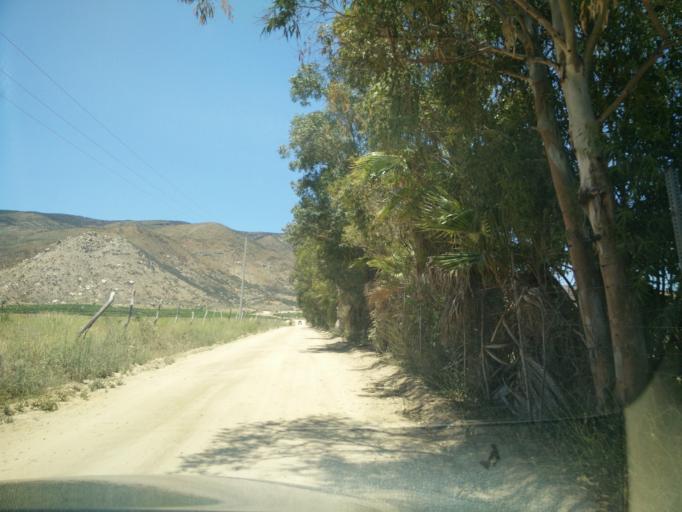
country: MX
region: Baja California
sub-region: Ensenada
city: Rancho Verde
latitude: 32.0491
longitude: -116.6635
